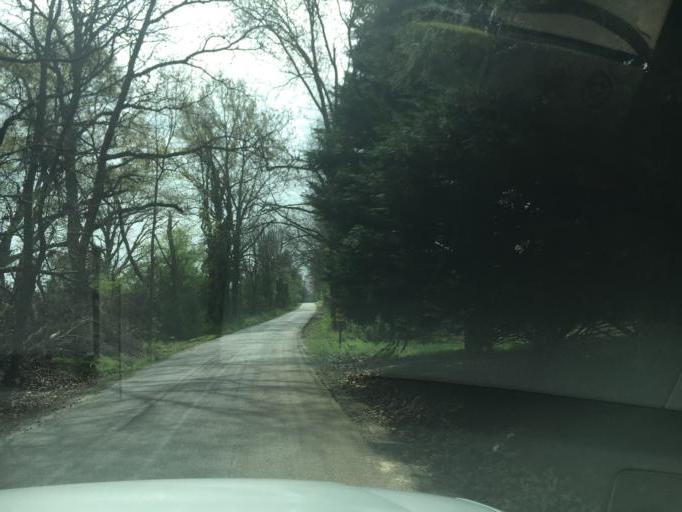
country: US
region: Georgia
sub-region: Hart County
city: Royston
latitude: 34.3573
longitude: -83.0454
